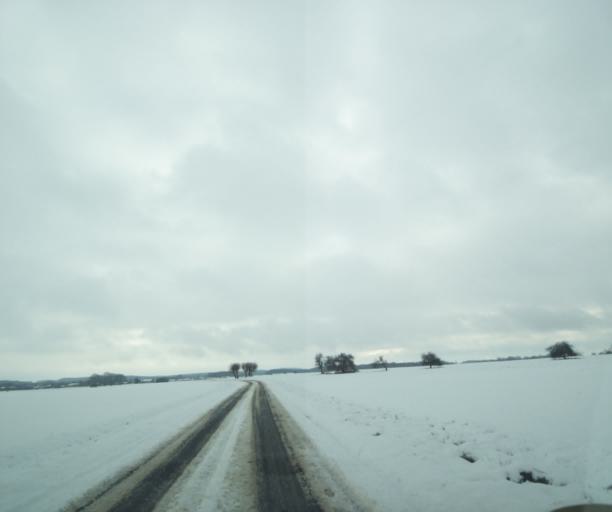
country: FR
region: Champagne-Ardenne
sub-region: Departement de la Haute-Marne
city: Montier-en-Der
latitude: 48.4995
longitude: 4.6869
